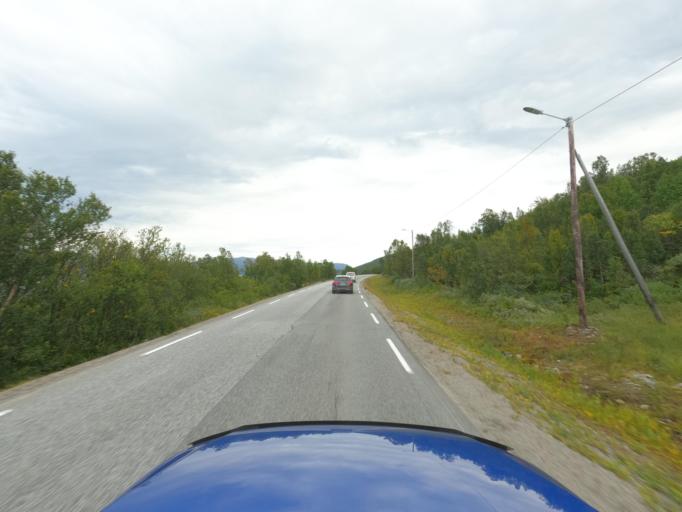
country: NO
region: Finnmark Fylke
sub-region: Kvalsund
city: Kvalsund
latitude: 70.4979
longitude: 24.0821
